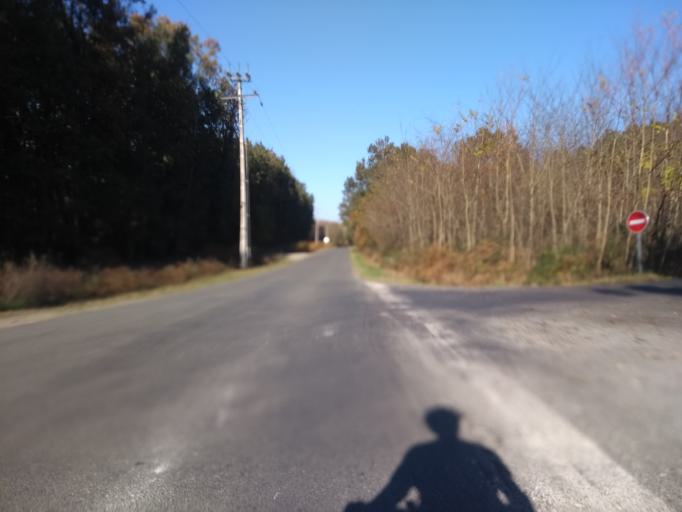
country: FR
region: Aquitaine
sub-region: Departement de la Gironde
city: Ayguemorte-les-Graves
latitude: 44.7012
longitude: -0.4810
